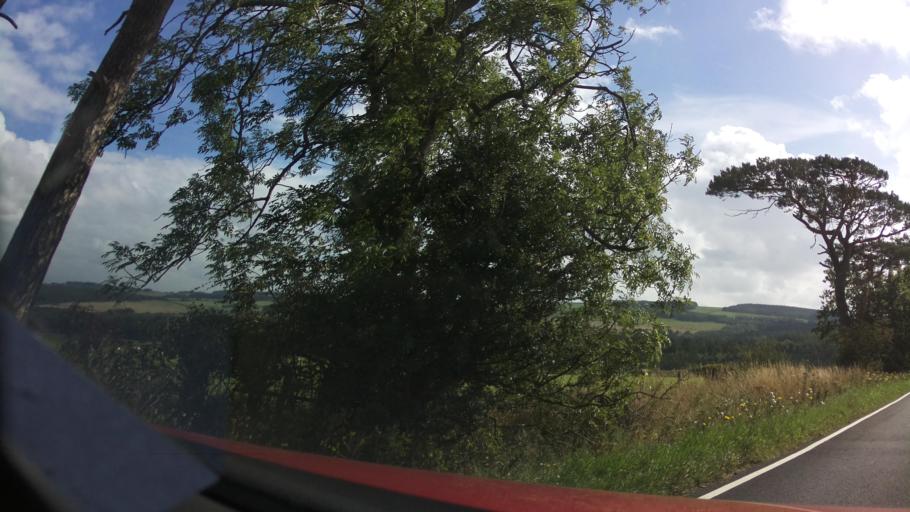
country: GB
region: England
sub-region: Northumberland
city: Healey
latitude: 54.9109
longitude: -1.9538
